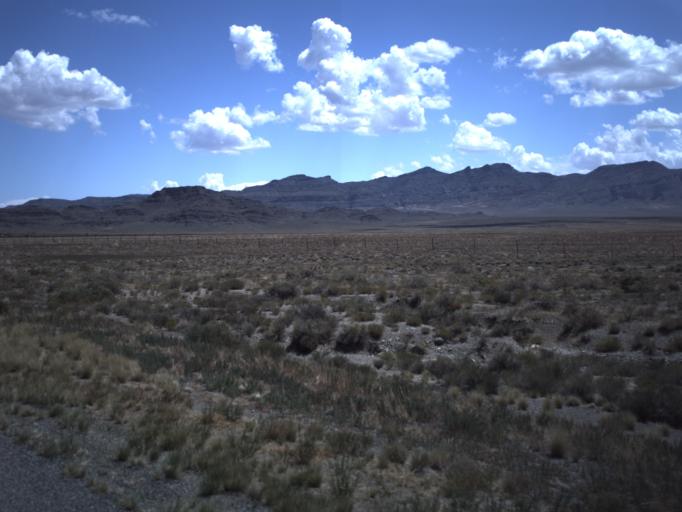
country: US
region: Utah
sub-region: Beaver County
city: Milford
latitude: 39.0571
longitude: -113.7655
